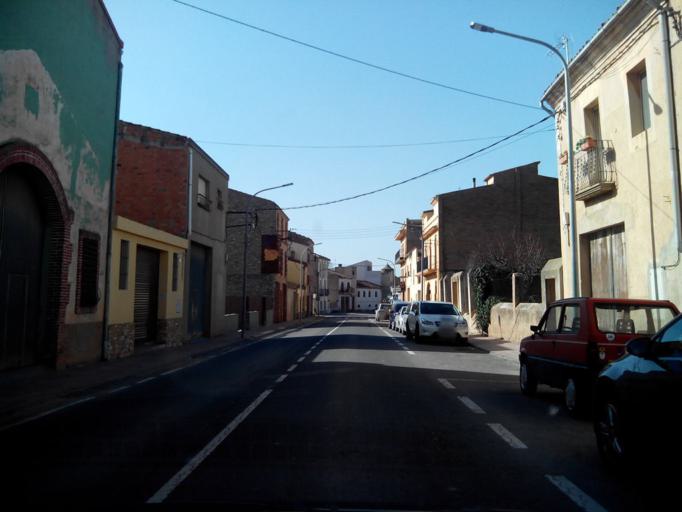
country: ES
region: Catalonia
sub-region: Provincia de Tarragona
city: Conesa
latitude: 41.4770
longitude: 1.2837
